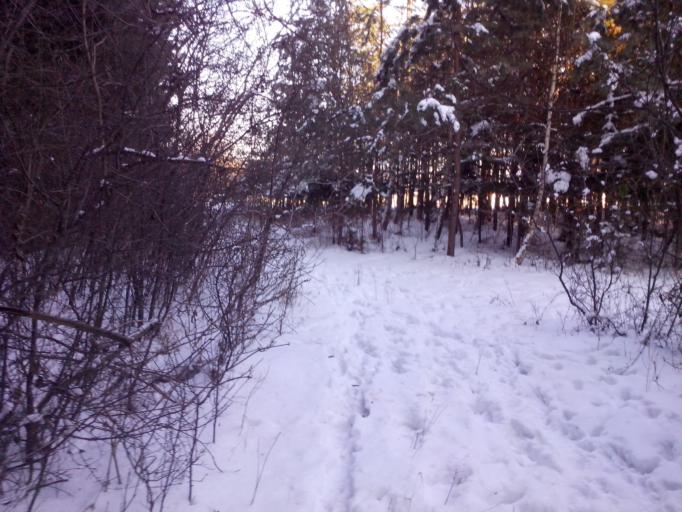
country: PL
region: Subcarpathian Voivodeship
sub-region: Powiat strzyzowski
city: Strzyzow
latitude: 49.8315
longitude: 21.8000
